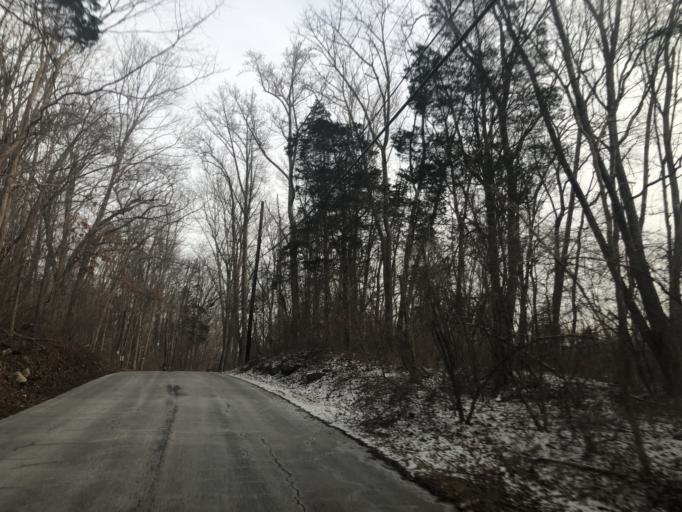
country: US
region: New Jersey
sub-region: Warren County
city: Oxford
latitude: 40.9172
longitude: -74.9693
